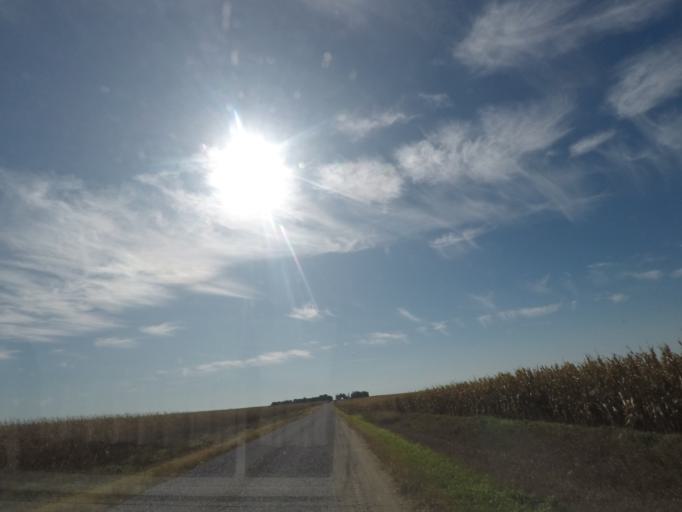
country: US
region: Iowa
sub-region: Story County
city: Nevada
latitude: 42.0601
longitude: -93.3291
